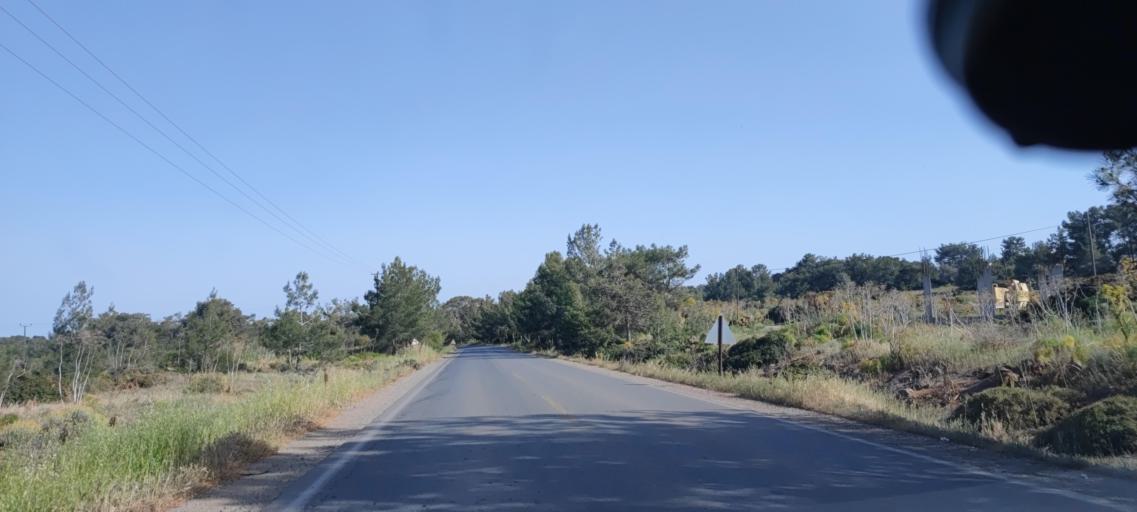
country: CY
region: Keryneia
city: Lapithos
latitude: 35.3110
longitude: 33.0590
